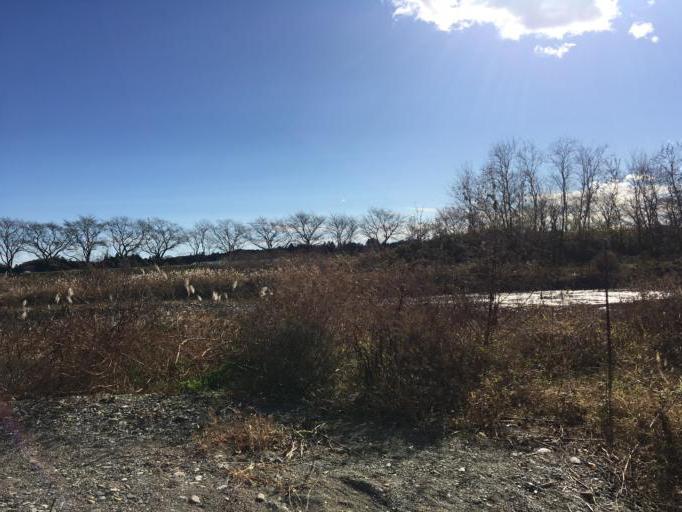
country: JP
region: Saitama
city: Ogawa
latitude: 36.0333
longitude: 139.3213
